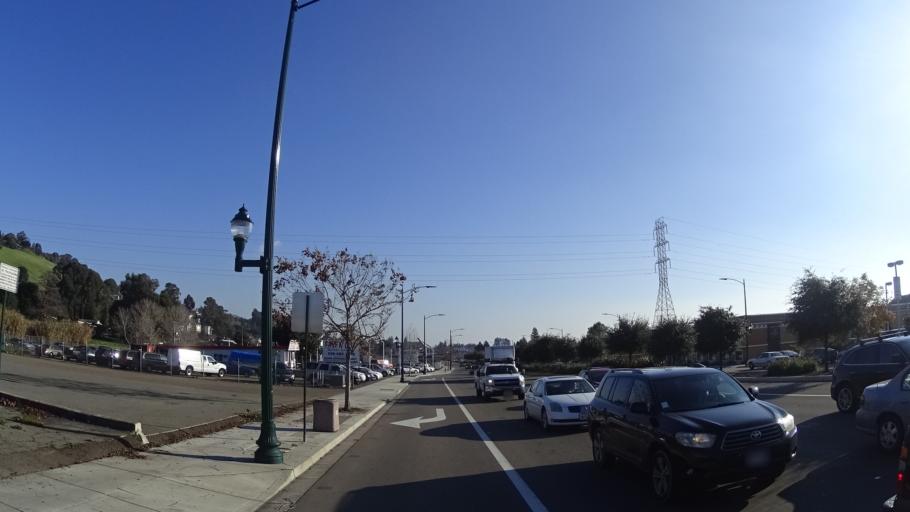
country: US
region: California
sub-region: Alameda County
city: Hayward
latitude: 37.6599
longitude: -122.0735
